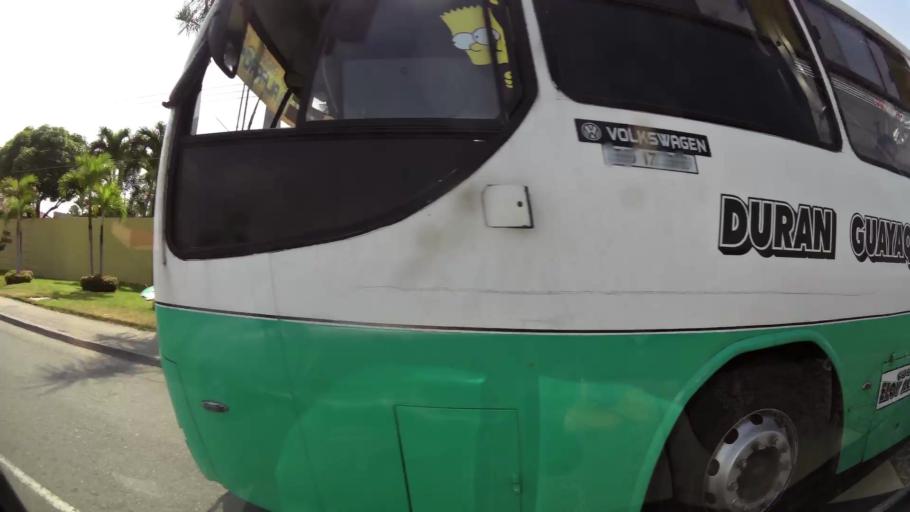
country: EC
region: Guayas
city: Eloy Alfaro
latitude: -2.1242
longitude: -79.8640
